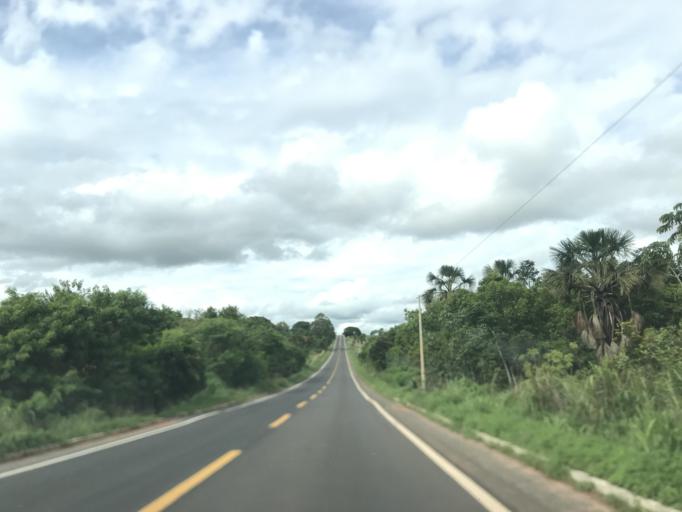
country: BR
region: Goias
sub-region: Piracanjuba
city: Piracanjuba
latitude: -17.1954
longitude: -48.6981
